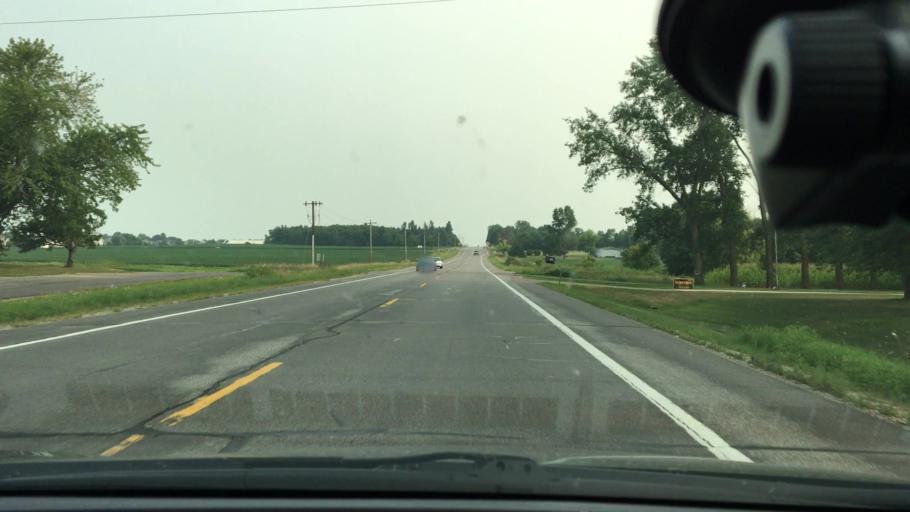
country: US
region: Minnesota
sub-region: Wright County
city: Albertville
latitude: 45.2602
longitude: -93.6634
